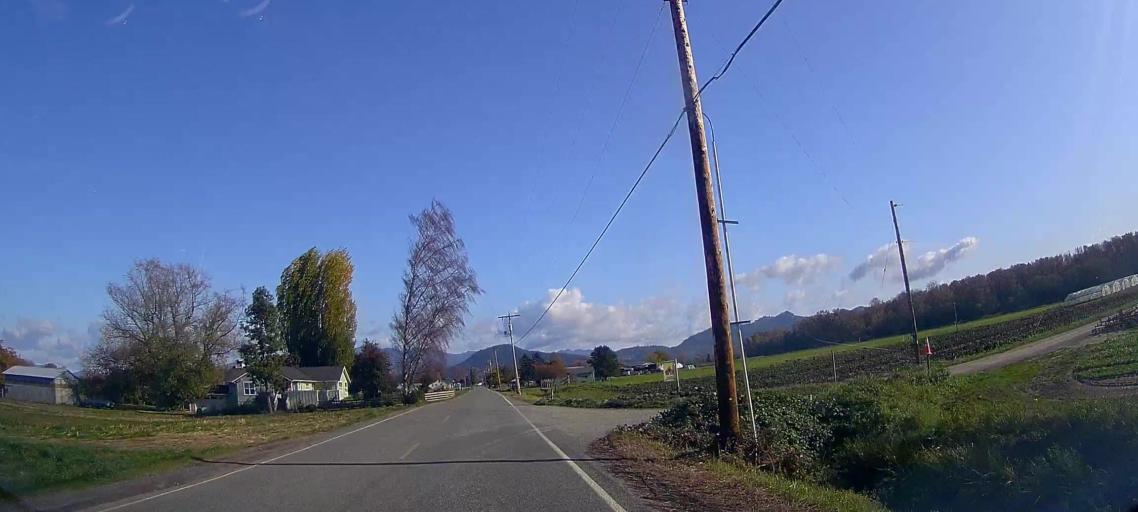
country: US
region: Washington
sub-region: Skagit County
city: Mount Vernon
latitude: 48.3991
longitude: -122.3802
